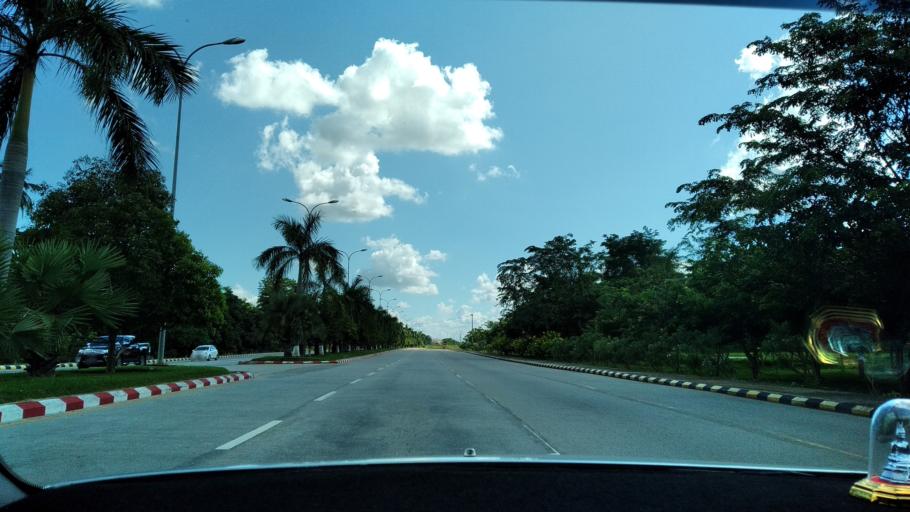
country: MM
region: Mandalay
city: Nay Pyi Taw
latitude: 19.7720
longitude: 96.1423
